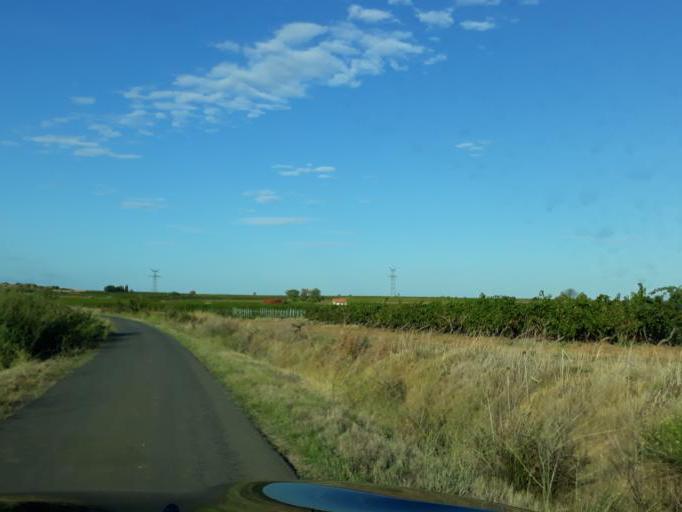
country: FR
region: Languedoc-Roussillon
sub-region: Departement de l'Herault
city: Florensac
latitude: 43.4057
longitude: 3.4745
